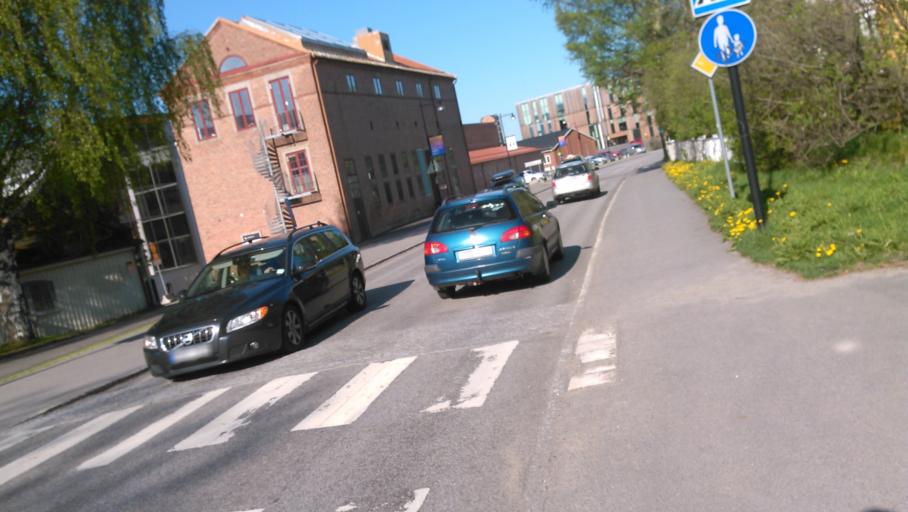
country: SE
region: Vaesterbotten
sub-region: Umea Kommun
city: Umea
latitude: 63.8213
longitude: 20.2776
